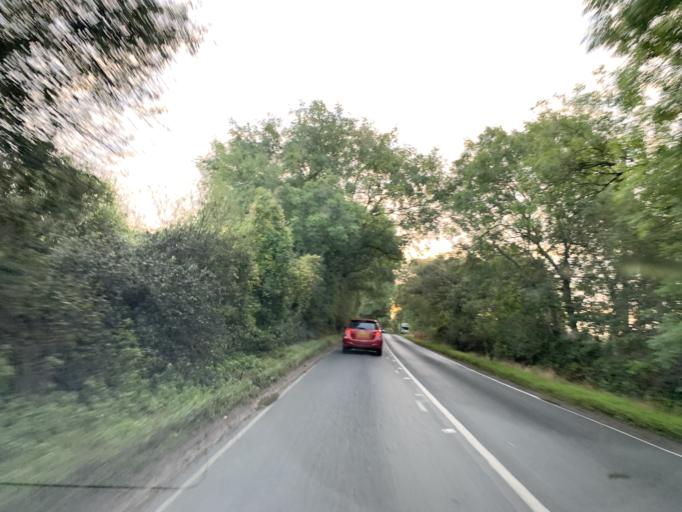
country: GB
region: England
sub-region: Hampshire
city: Romsey
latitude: 50.9868
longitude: -1.5265
